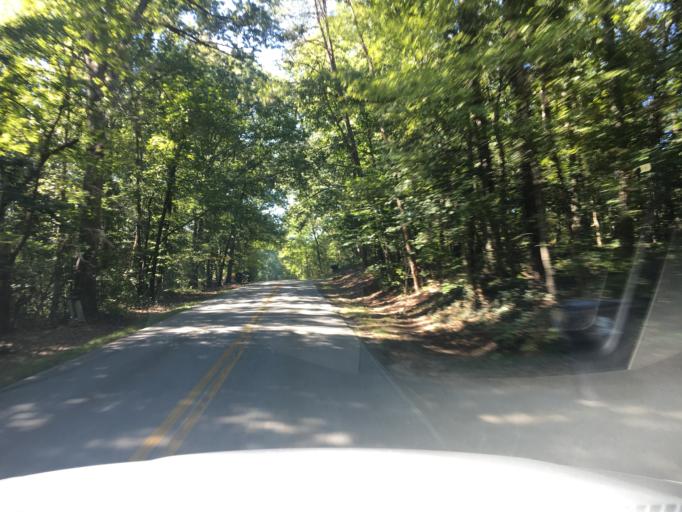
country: US
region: South Carolina
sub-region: Greenville County
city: Taylors
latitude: 34.8966
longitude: -82.2742
